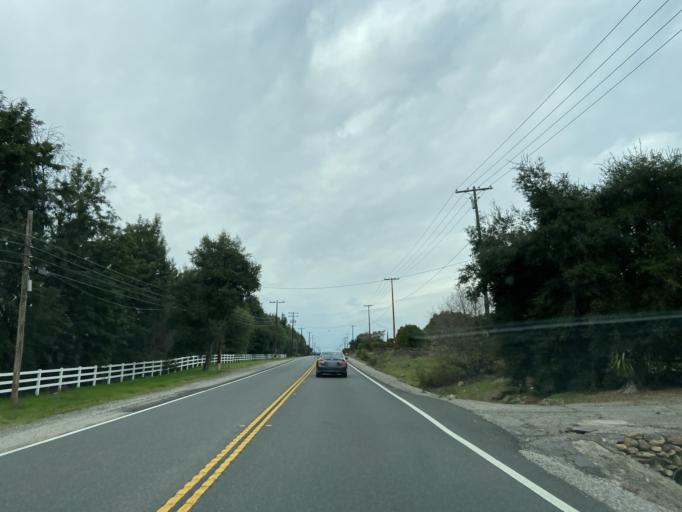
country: US
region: California
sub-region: San Diego County
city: Valley Center
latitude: 33.3061
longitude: -116.9811
